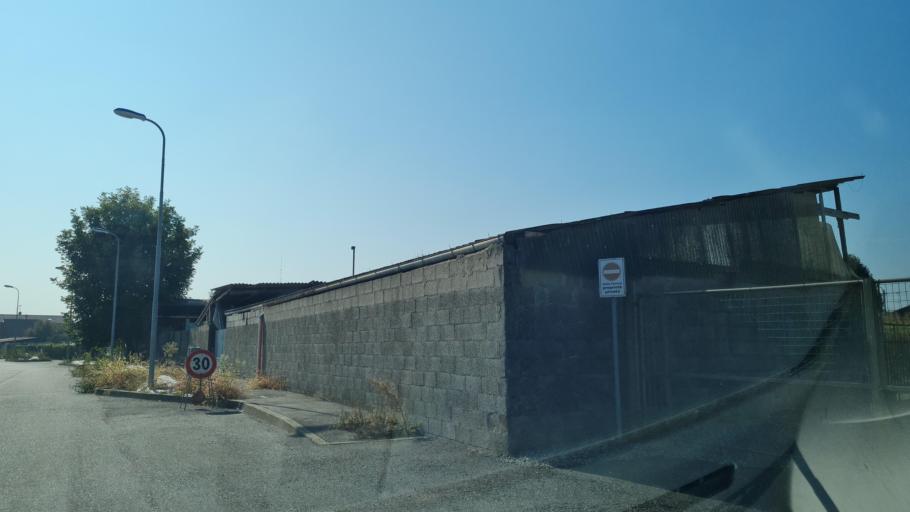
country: IT
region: Piedmont
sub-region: Provincia di Novara
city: Carpignano Sesia
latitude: 45.5309
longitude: 8.4178
